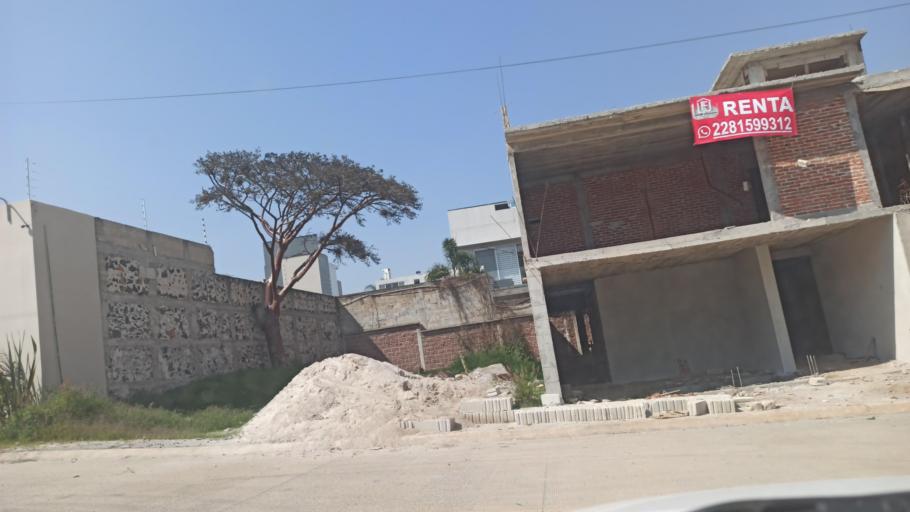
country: MX
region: Veracruz
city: El Castillo
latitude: 19.5284
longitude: -96.8640
